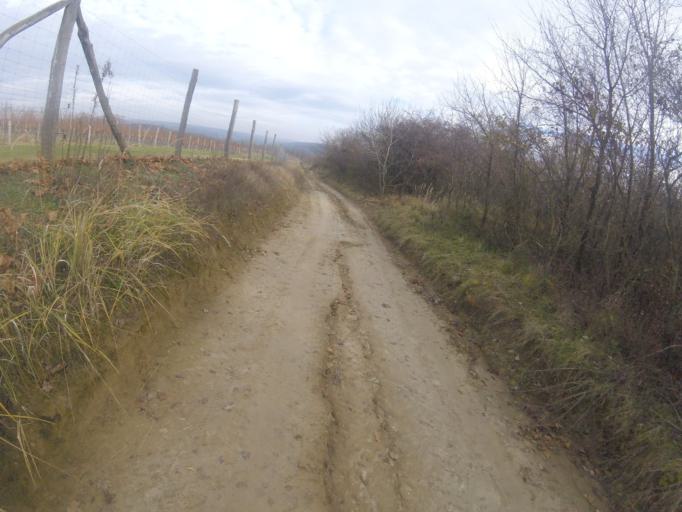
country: HU
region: Tolna
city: Bonyhad
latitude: 46.2474
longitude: 18.5984
